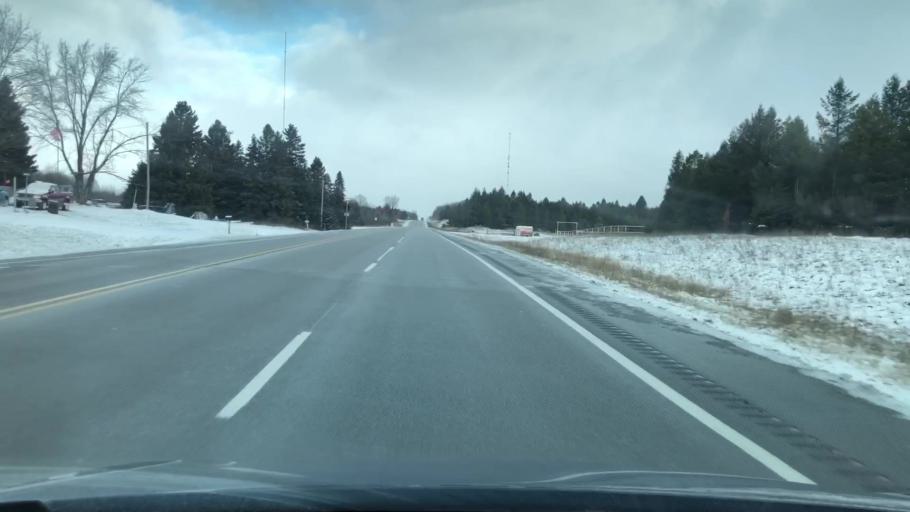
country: US
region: Michigan
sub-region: Grand Traverse County
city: Kingsley
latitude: 44.4465
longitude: -85.6980
